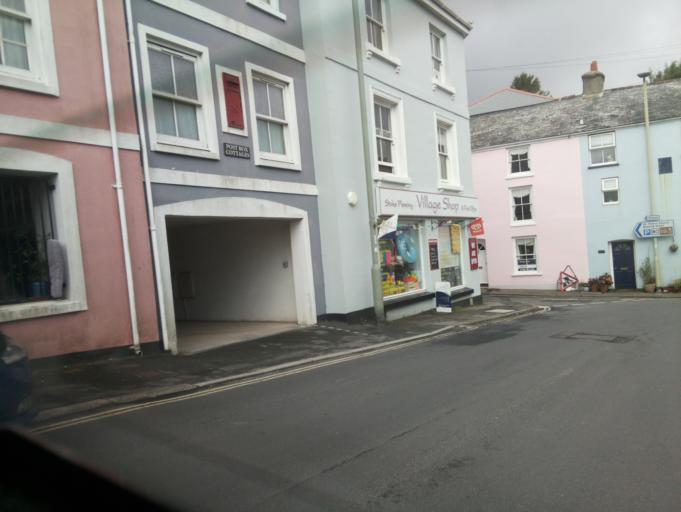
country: GB
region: England
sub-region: Devon
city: Dartmouth
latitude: 50.3244
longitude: -3.5992
